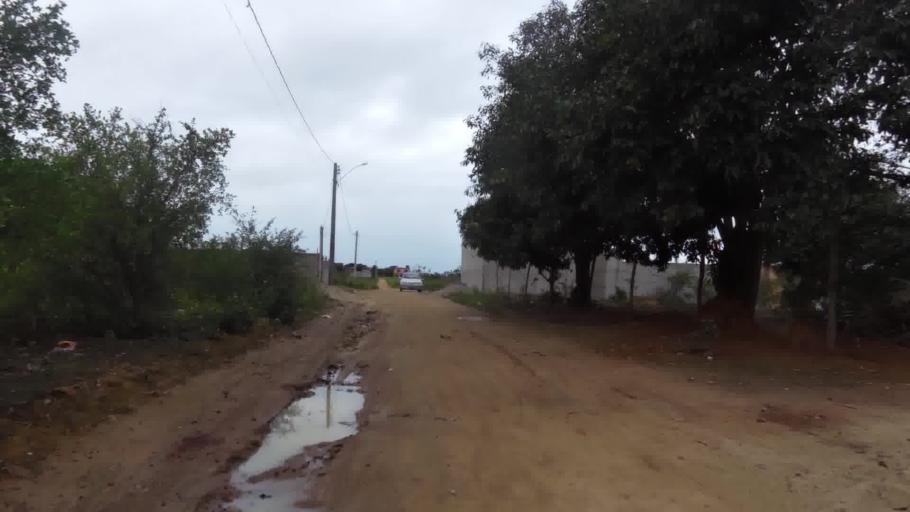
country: BR
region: Espirito Santo
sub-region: Marataizes
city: Marataizes
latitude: -21.0495
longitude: -40.8416
